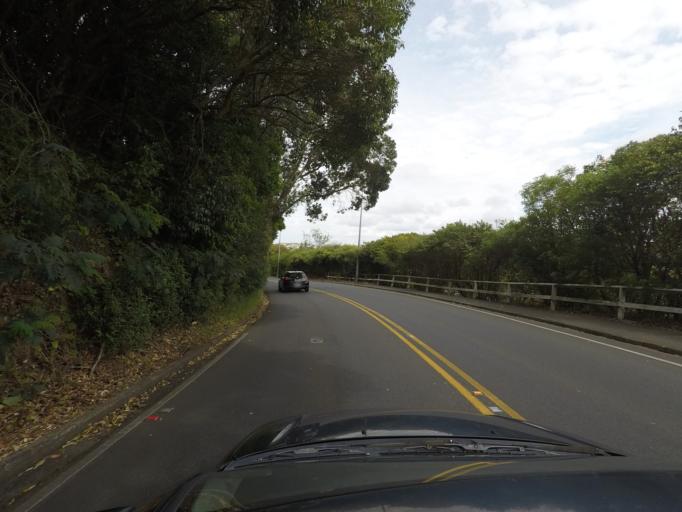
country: NZ
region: Auckland
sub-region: Auckland
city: Auckland
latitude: -36.8597
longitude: 174.8111
